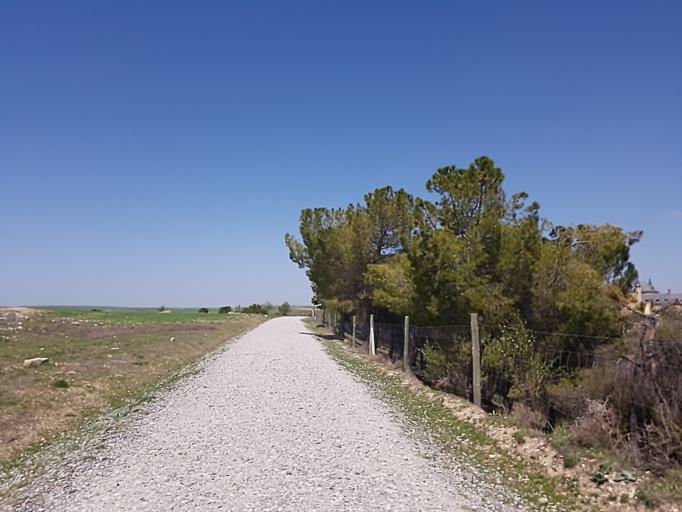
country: ES
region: Castille and Leon
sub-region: Provincia de Segovia
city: Segovia
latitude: 40.9500
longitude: -4.1343
